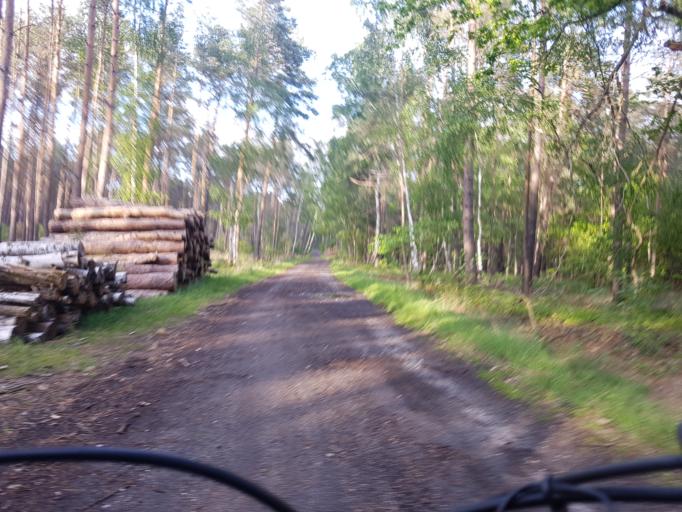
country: DE
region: Brandenburg
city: Trobitz
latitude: 51.5654
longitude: 13.4294
